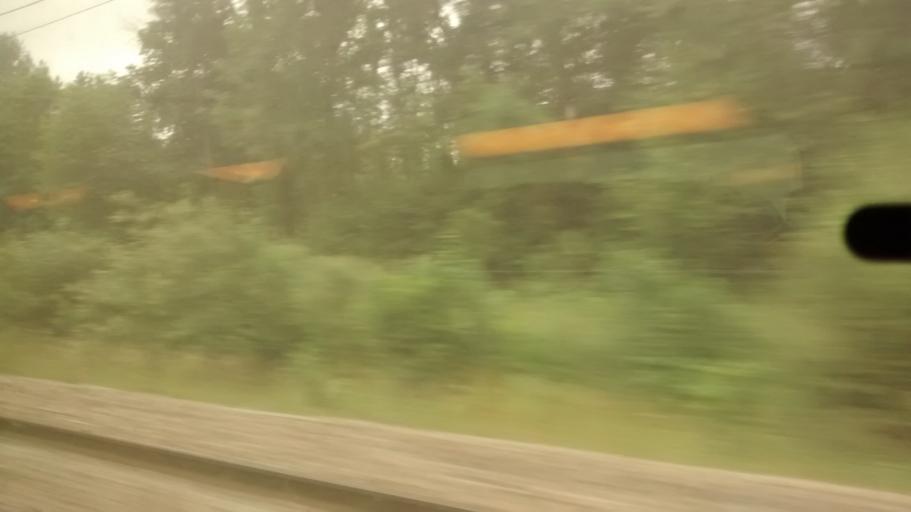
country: FR
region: Bourgogne
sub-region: Departement de l'Yonne
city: Brienon-sur-Armancon
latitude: 48.0003
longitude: 3.6512
